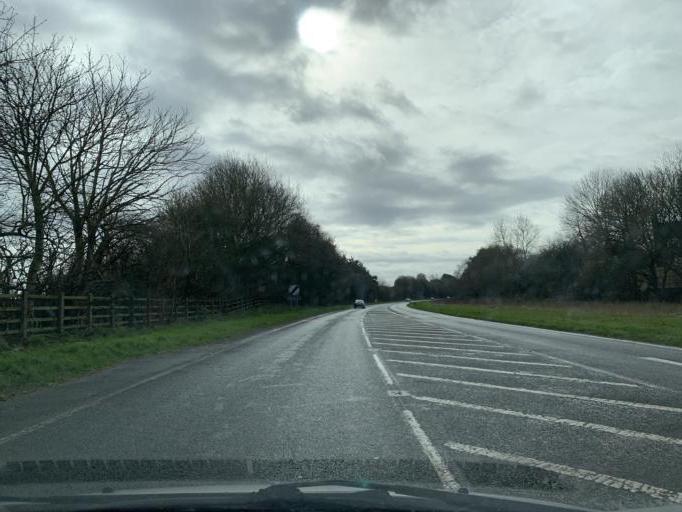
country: GB
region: England
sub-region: Hampshire
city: Fordingbridge
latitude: 50.9365
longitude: -1.7850
